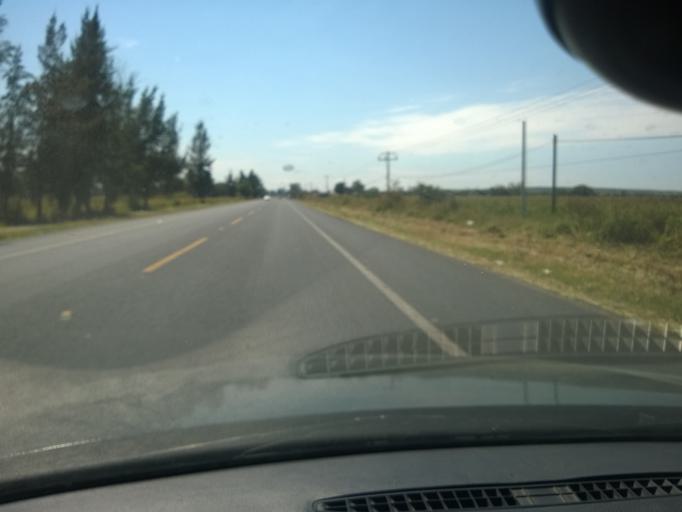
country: MX
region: Guanajuato
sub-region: Leon
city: El CERESO
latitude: 21.0060
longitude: -101.7016
